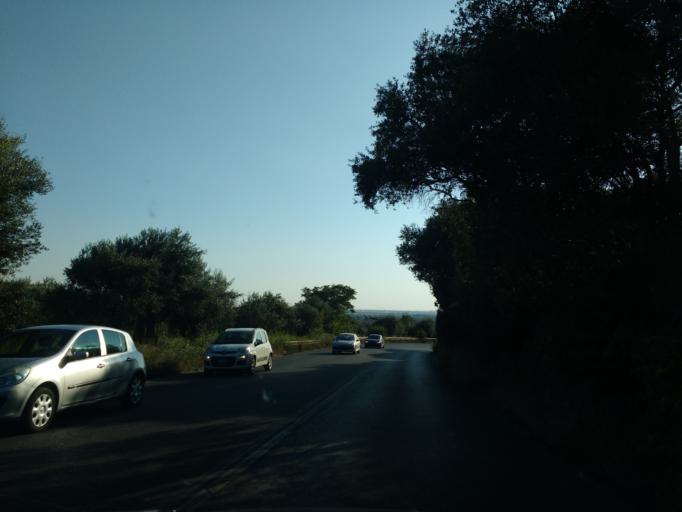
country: IT
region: Latium
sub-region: Citta metropolitana di Roma Capitale
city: Villa Adriana
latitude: 41.9543
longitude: 12.7854
